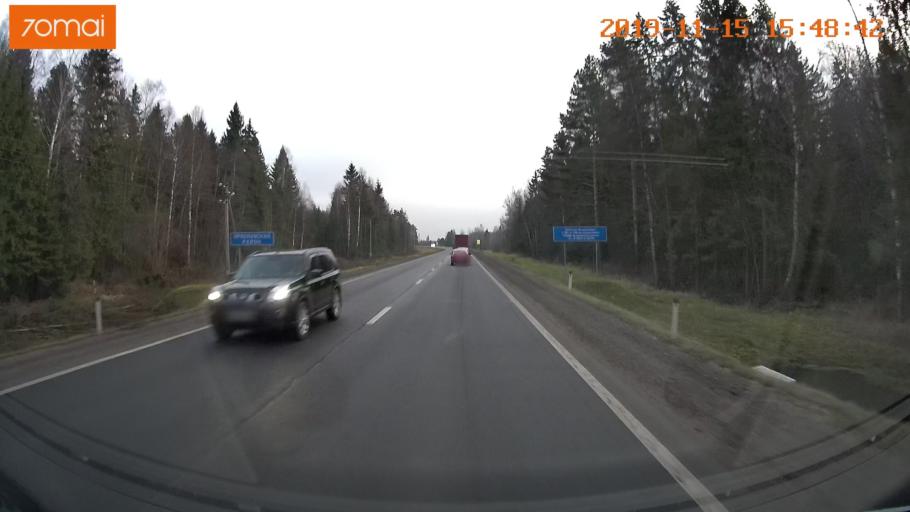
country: RU
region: Jaroslavl
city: Danilov
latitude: 57.9242
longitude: 40.0066
